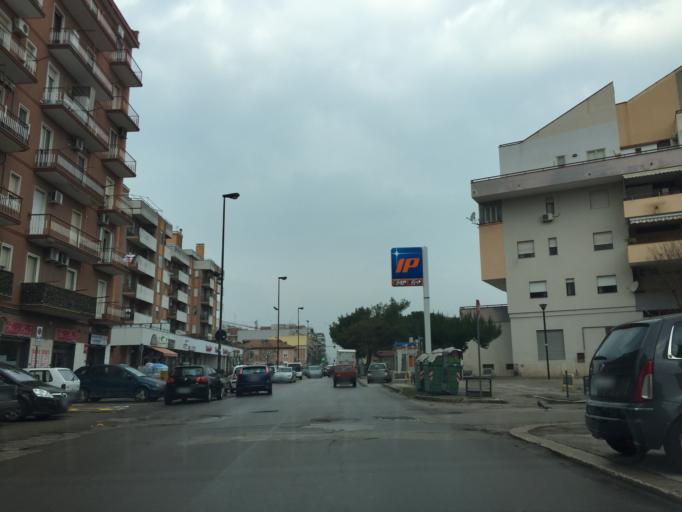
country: IT
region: Apulia
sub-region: Provincia di Foggia
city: Foggia
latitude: 41.4658
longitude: 15.5360
